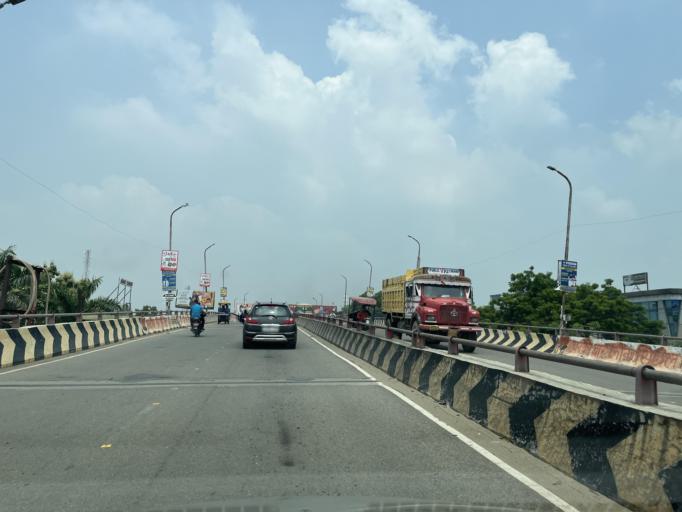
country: IN
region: Uttar Pradesh
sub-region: Bijnor
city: Najibabad
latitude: 29.6042
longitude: 78.3436
